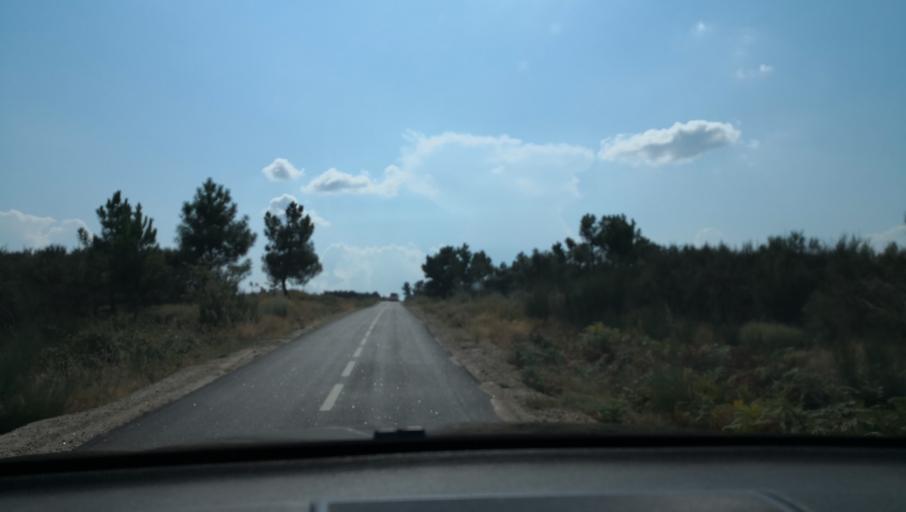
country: PT
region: Vila Real
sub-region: Sabrosa
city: Sabrosa
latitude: 41.2918
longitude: -7.6128
